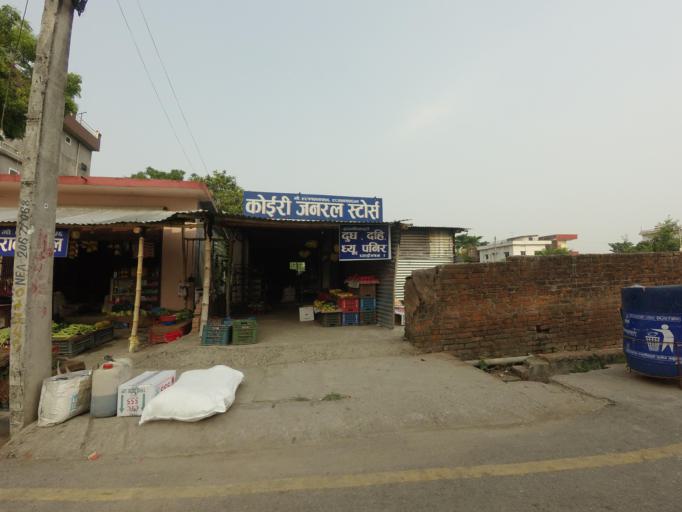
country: NP
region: Western Region
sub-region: Lumbini Zone
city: Bhairahawa
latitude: 27.5256
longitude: 83.4592
